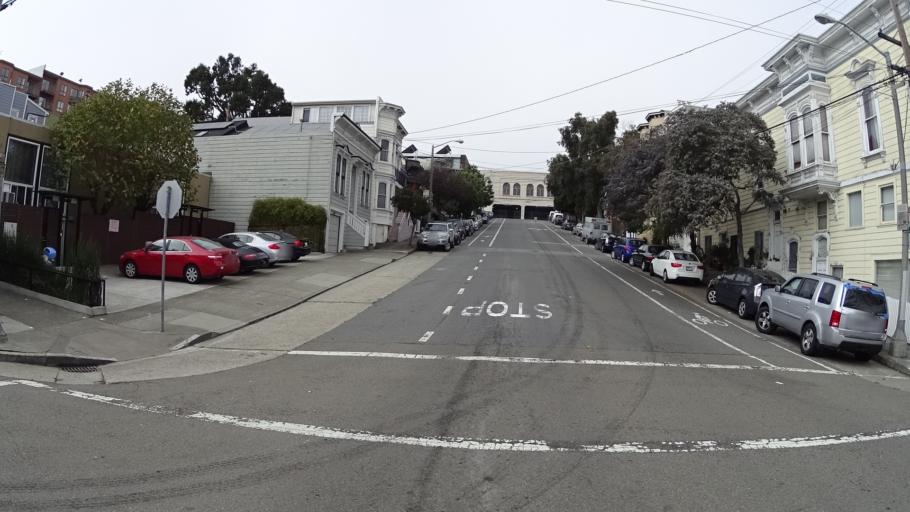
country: US
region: California
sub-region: San Francisco County
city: San Francisco
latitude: 37.7837
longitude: -122.4447
